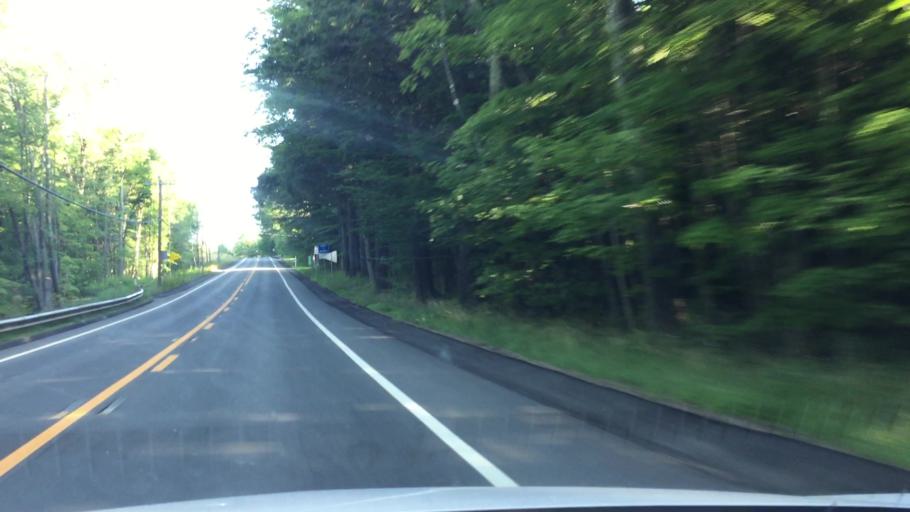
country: US
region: Massachusetts
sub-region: Berkshire County
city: Becket
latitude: 42.2708
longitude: -73.0536
